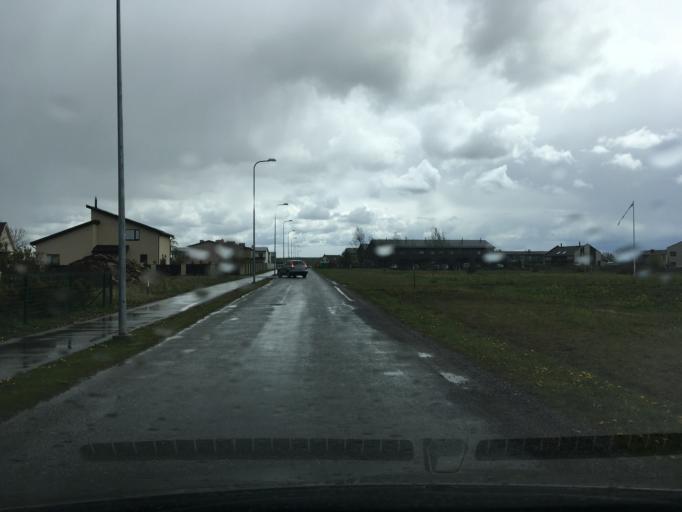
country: EE
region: Harju
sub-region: Joelaehtme vald
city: Loo
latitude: 59.4441
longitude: 24.9606
